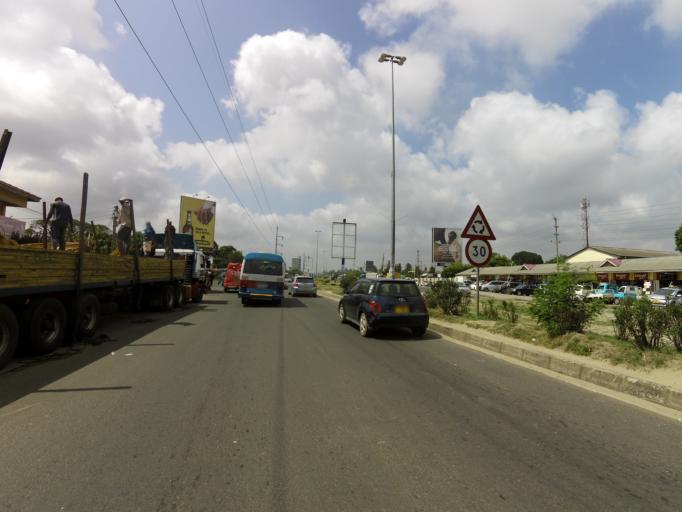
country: TZ
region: Dar es Salaam
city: Magomeni
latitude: -6.7662
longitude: 39.2280
